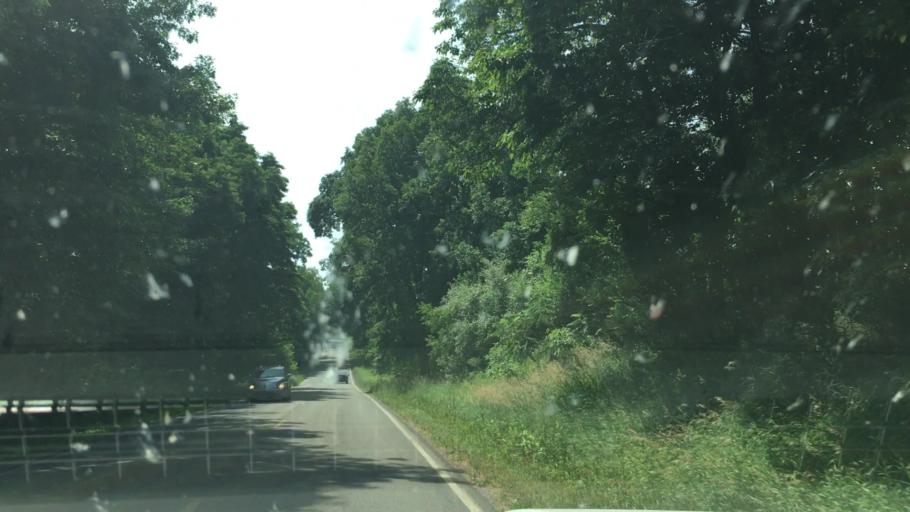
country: US
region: Michigan
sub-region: Kalamazoo County
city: Comstock Northwest
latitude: 42.4287
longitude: -85.5145
